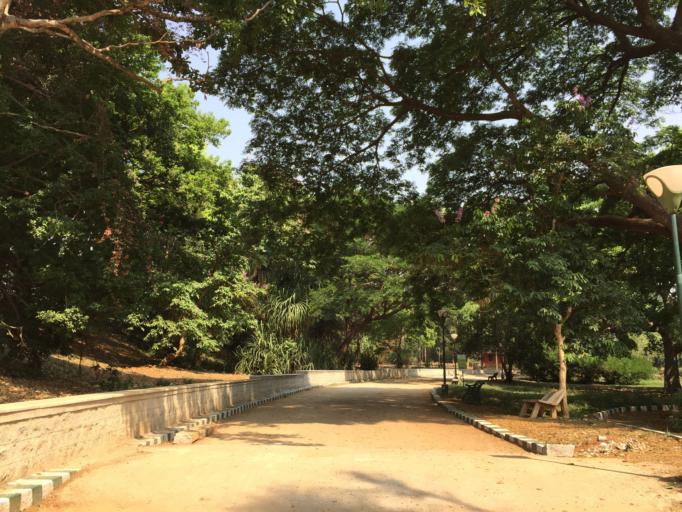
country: IN
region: Karnataka
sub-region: Bangalore Urban
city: Bangalore
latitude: 12.9476
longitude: 77.5835
